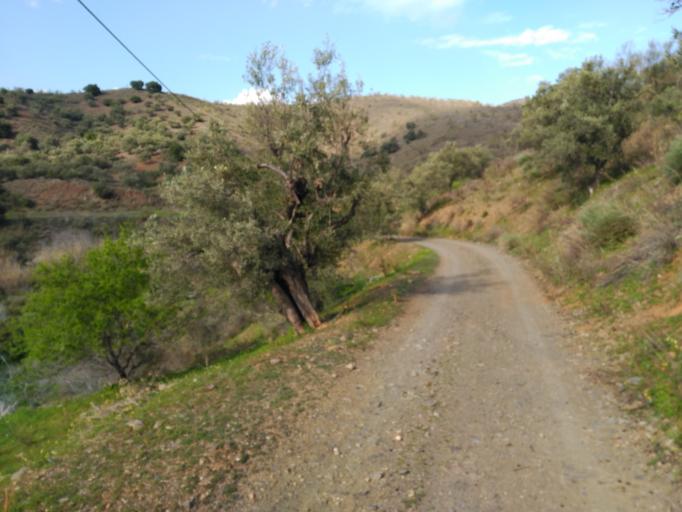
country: ES
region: Andalusia
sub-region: Provincia de Malaga
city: Valdes
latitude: 36.7367
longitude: -4.2244
